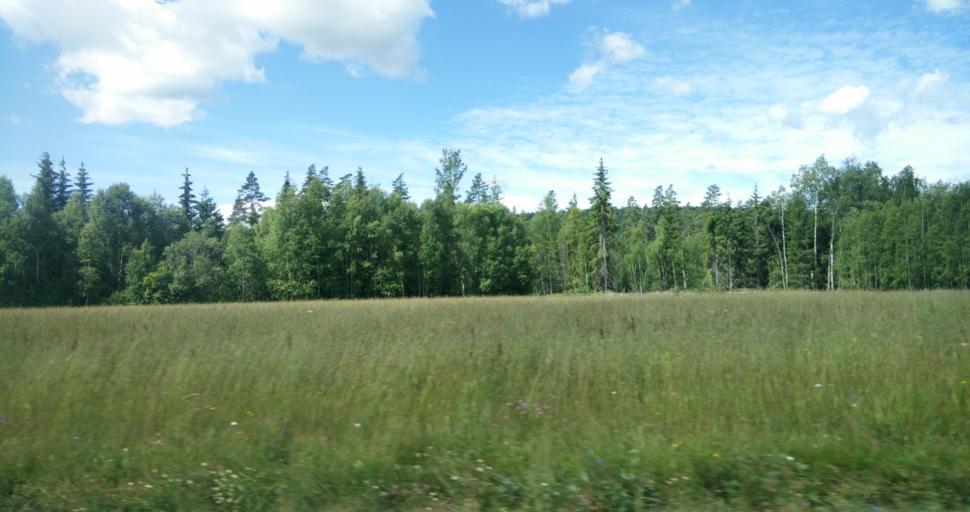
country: SE
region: Vaermland
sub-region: Hagfors Kommun
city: Ekshaerad
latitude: 60.0444
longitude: 13.4931
